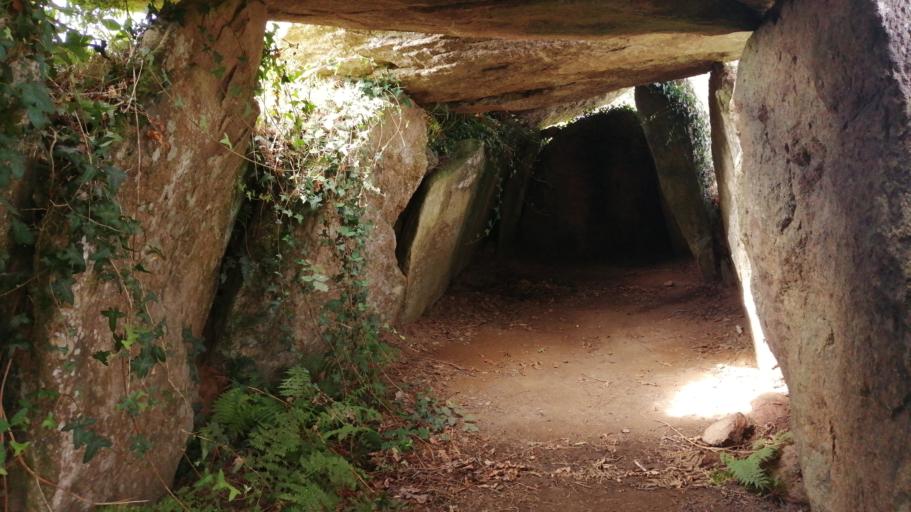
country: FR
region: Brittany
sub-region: Departement du Finistere
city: Poullan-sur-Mer
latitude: 48.0833
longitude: -4.4546
